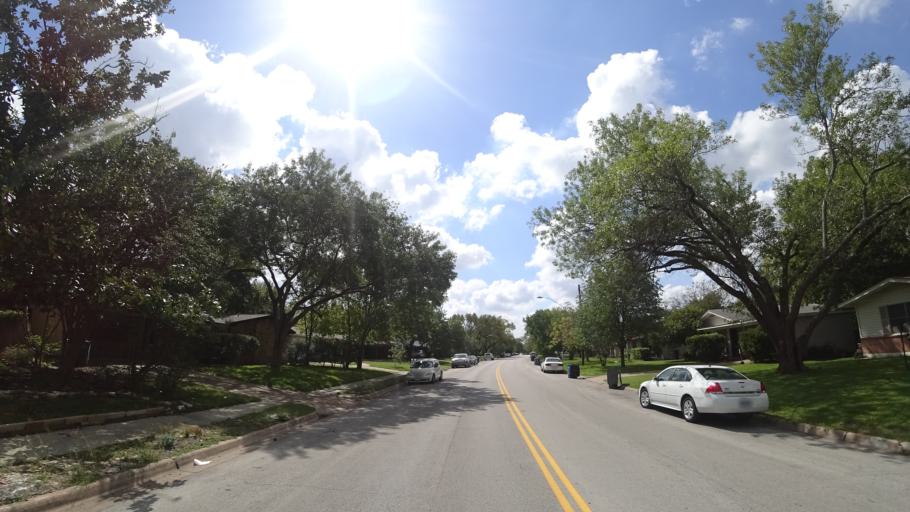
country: US
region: Texas
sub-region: Travis County
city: Austin
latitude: 30.3582
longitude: -97.7211
